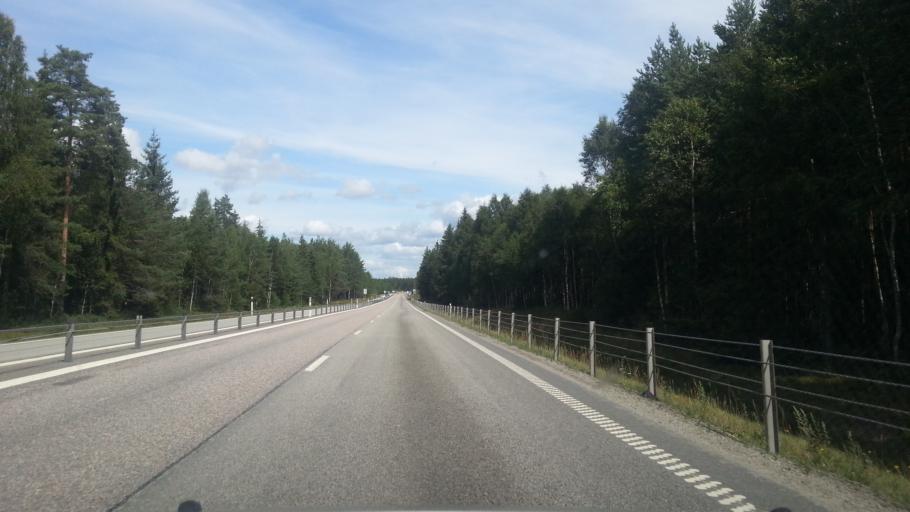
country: SE
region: OErebro
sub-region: Lindesbergs Kommun
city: Lindesberg
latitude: 59.5350
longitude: 15.2006
